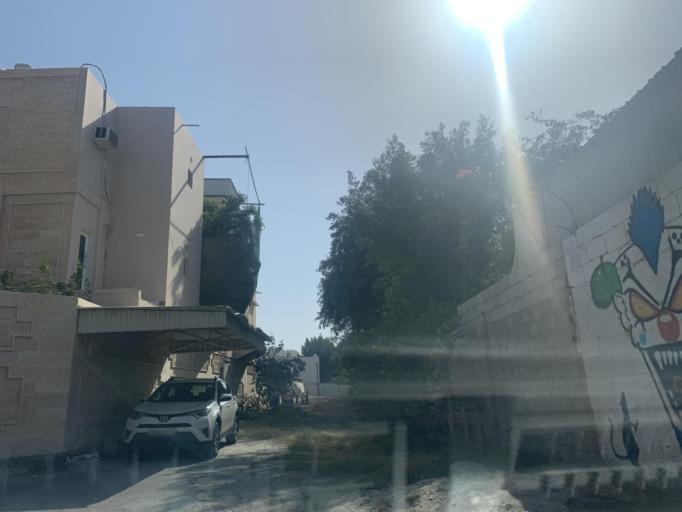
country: BH
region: Manama
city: Jidd Hafs
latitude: 26.2120
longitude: 50.4545
